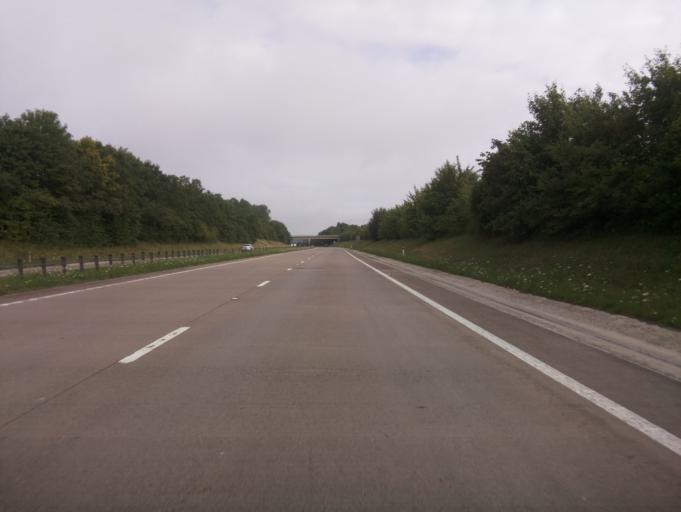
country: GB
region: England
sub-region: Gloucestershire
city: Cirencester
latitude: 51.7086
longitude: -1.9286
